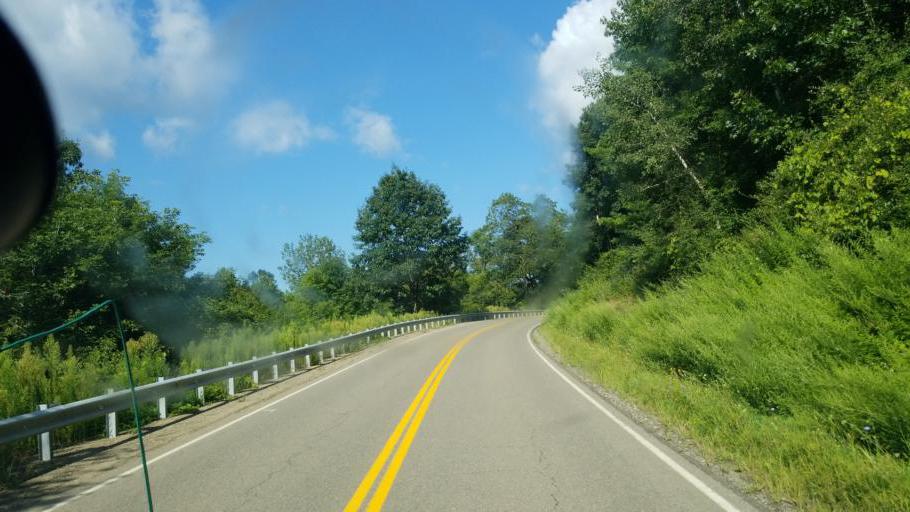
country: US
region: New York
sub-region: Steuben County
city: Canisteo
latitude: 42.2663
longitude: -77.5841
